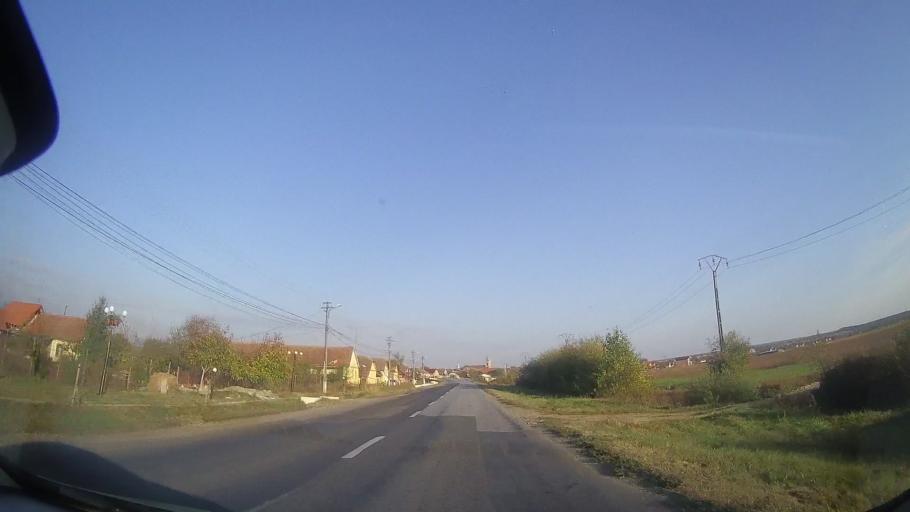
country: RO
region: Timis
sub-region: Comuna Pischia
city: Pischia
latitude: 45.8976
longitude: 21.3429
